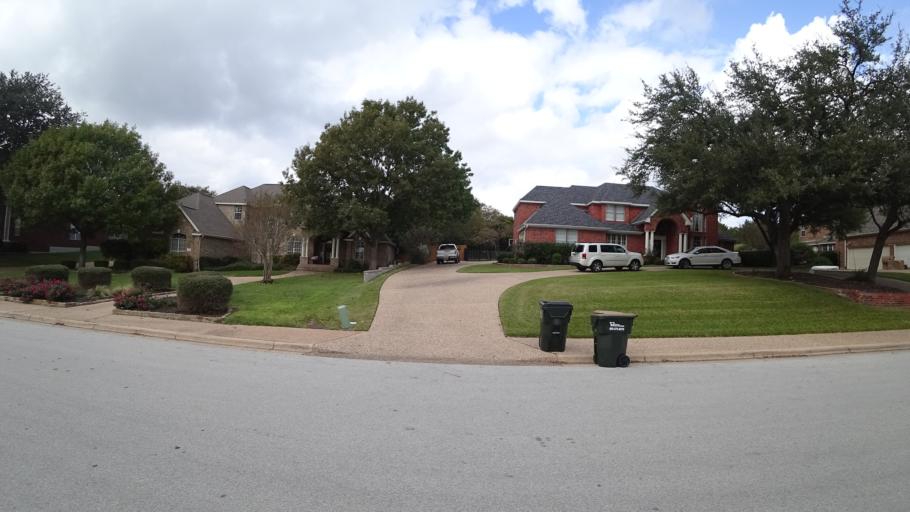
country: US
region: Texas
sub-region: Travis County
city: Barton Creek
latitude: 30.2974
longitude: -97.8950
